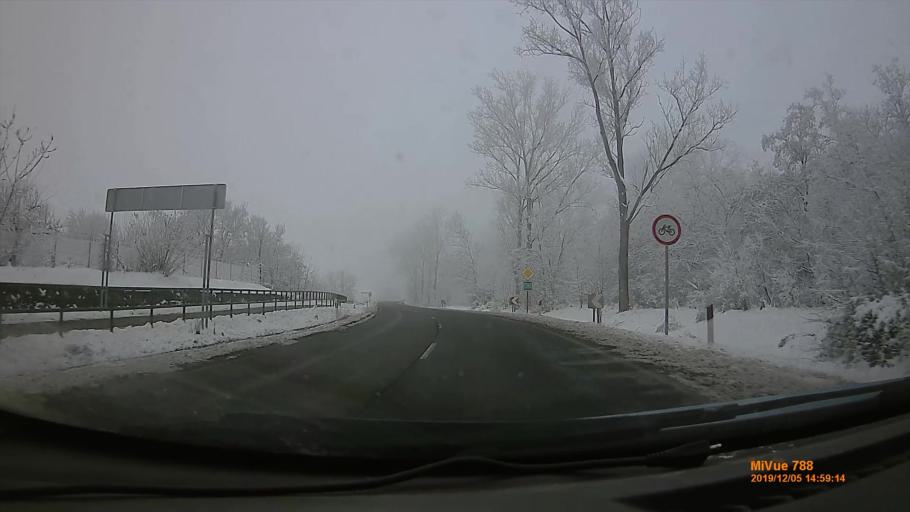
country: HU
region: Szabolcs-Szatmar-Bereg
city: Nyirtelek
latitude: 48.0556
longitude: 21.5601
